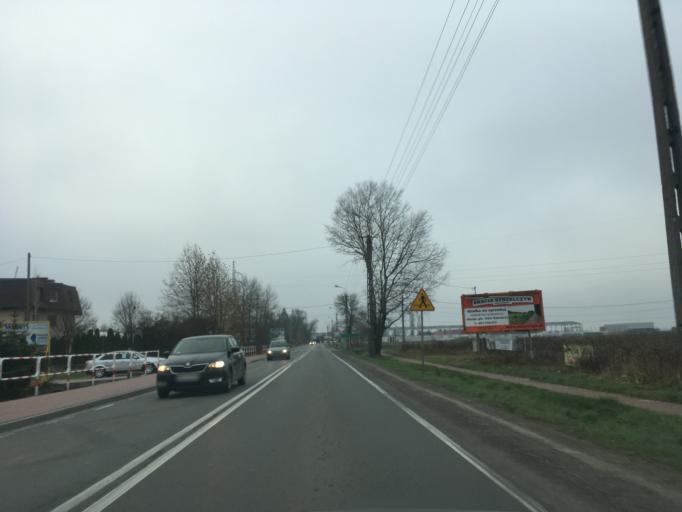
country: PL
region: Masovian Voivodeship
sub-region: Powiat piaseczynski
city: Lesznowola
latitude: 52.0809
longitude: 20.9774
